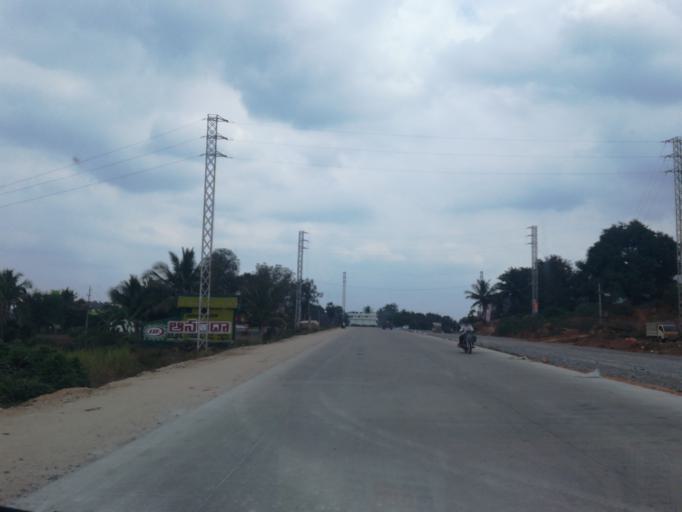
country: IN
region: Andhra Pradesh
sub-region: Chittoor
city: Ramapuram
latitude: 13.0955
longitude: 79.1289
